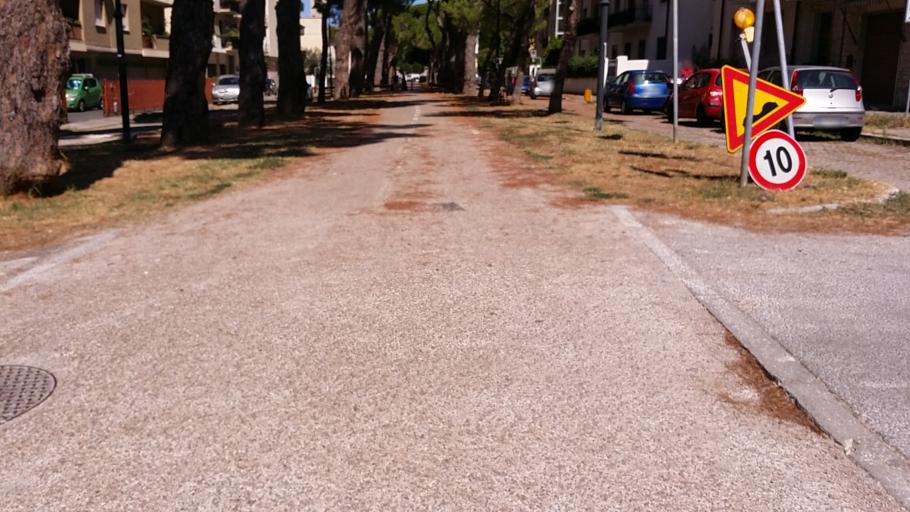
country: IT
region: Tuscany
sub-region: Provincia di Livorno
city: Livorno
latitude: 43.5342
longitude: 10.3194
